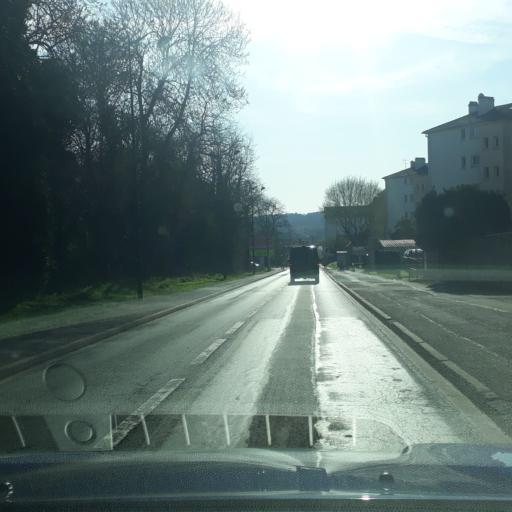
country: FR
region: Ile-de-France
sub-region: Departement de l'Essonne
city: Etampes
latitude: 48.4401
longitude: 2.1561
